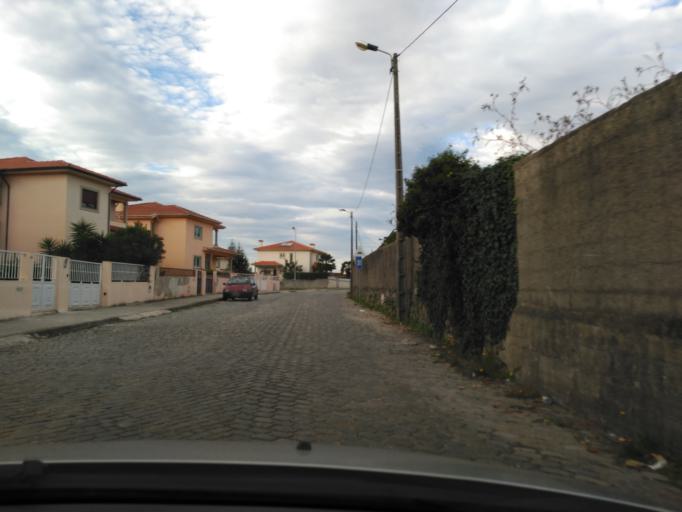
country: PT
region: Braga
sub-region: Braga
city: Braga
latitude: 41.5552
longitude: -8.4450
